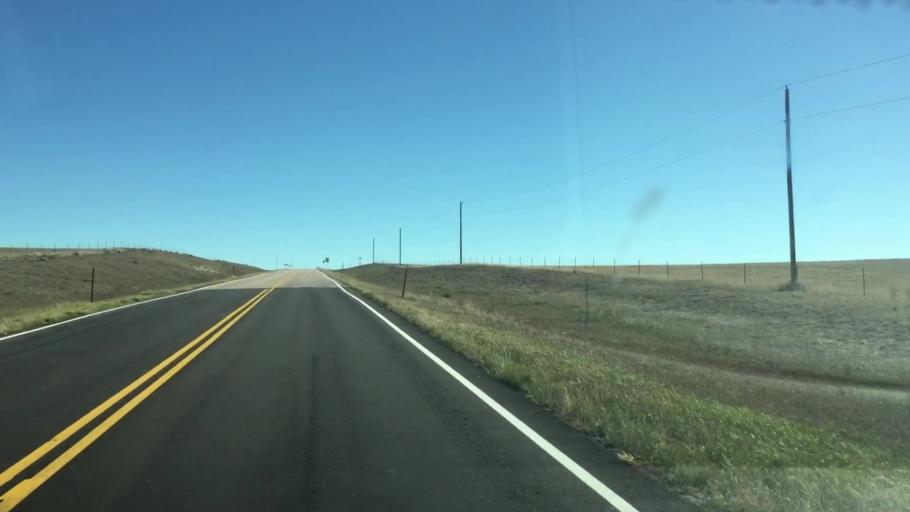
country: US
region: Colorado
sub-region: Lincoln County
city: Limon
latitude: 39.3094
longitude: -103.8323
